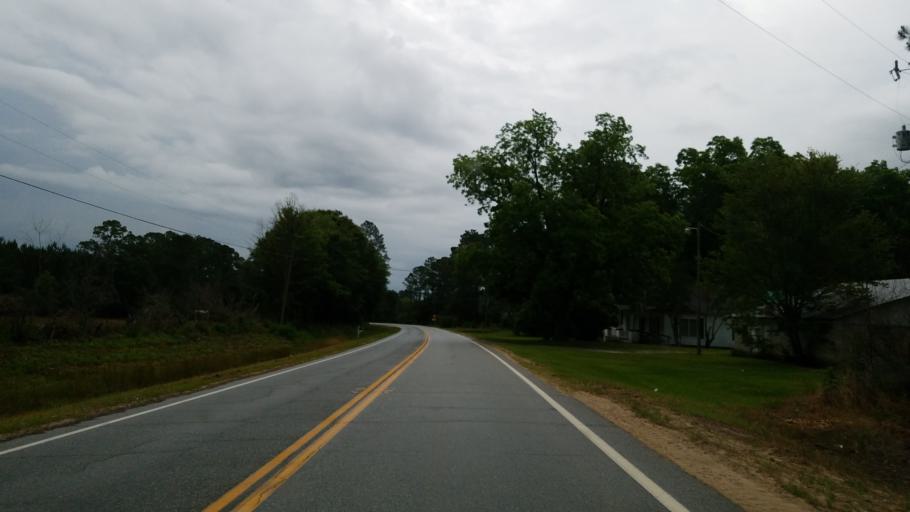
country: US
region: Georgia
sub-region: Berrien County
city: Ray City
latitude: 31.0743
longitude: -83.2122
